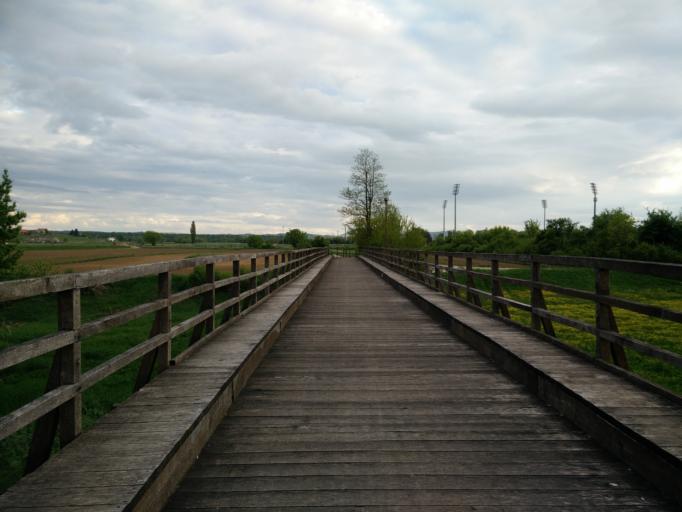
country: HR
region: Karlovacka
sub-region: Grad Karlovac
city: Karlovac
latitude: 45.4892
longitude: 15.5649
